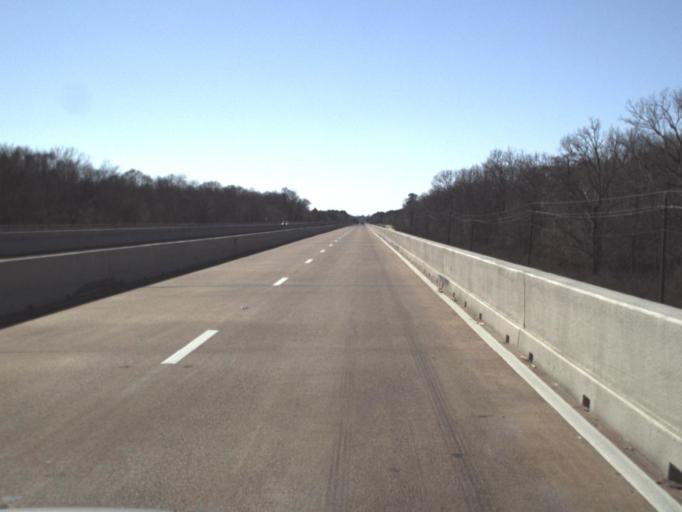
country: US
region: Florida
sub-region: Calhoun County
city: Blountstown
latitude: 30.4432
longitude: -85.0107
